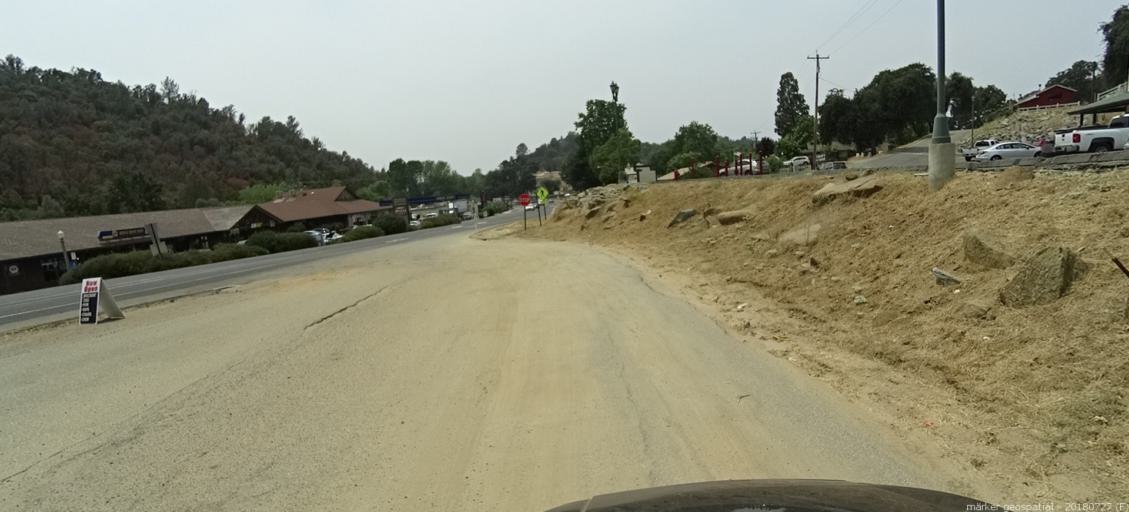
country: US
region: California
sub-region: Madera County
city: Coarsegold
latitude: 37.2628
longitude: -119.6980
